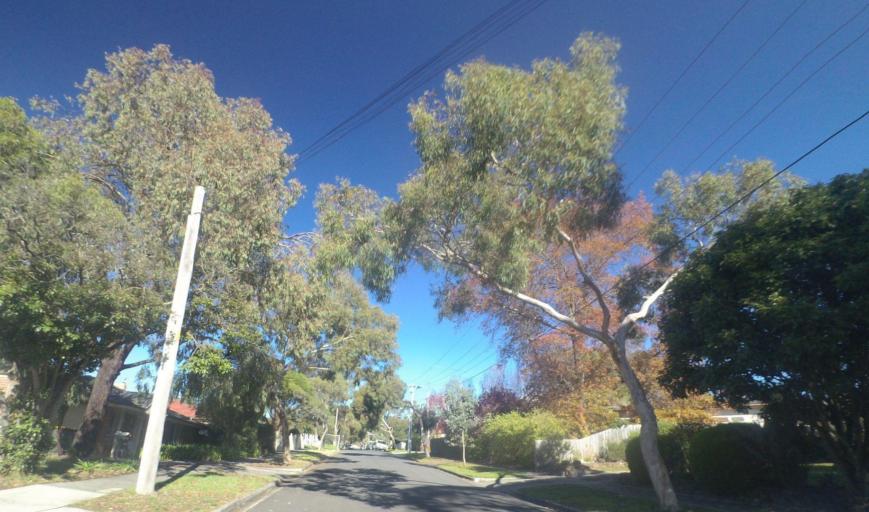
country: AU
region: Victoria
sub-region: Whitehorse
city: Box Hill North
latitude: -37.8052
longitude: 145.1239
